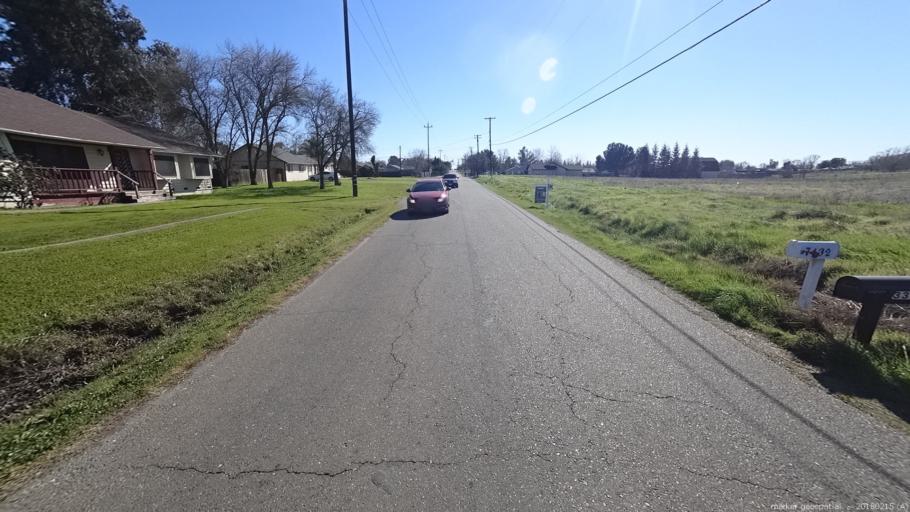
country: US
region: California
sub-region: Sacramento County
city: North Highlands
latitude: 38.7021
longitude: -121.3875
